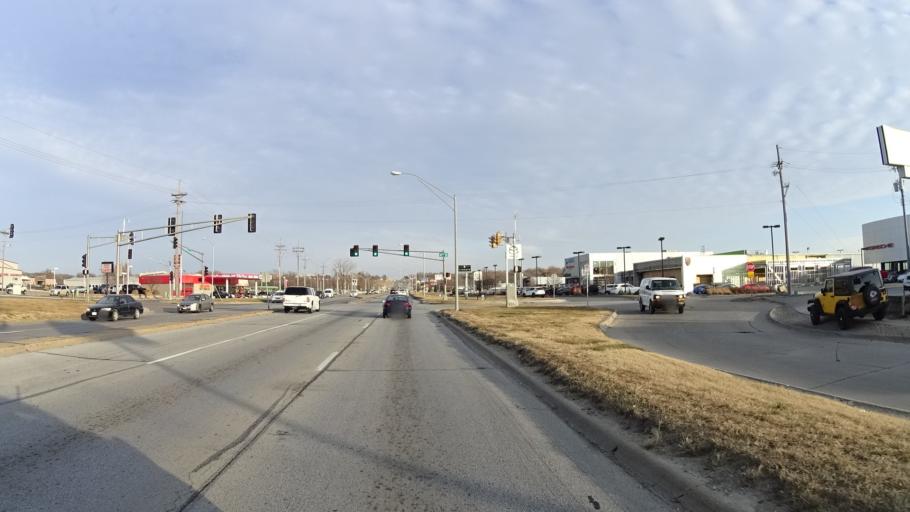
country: US
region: Nebraska
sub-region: Douglas County
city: Ralston
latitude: 41.2124
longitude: -96.0162
